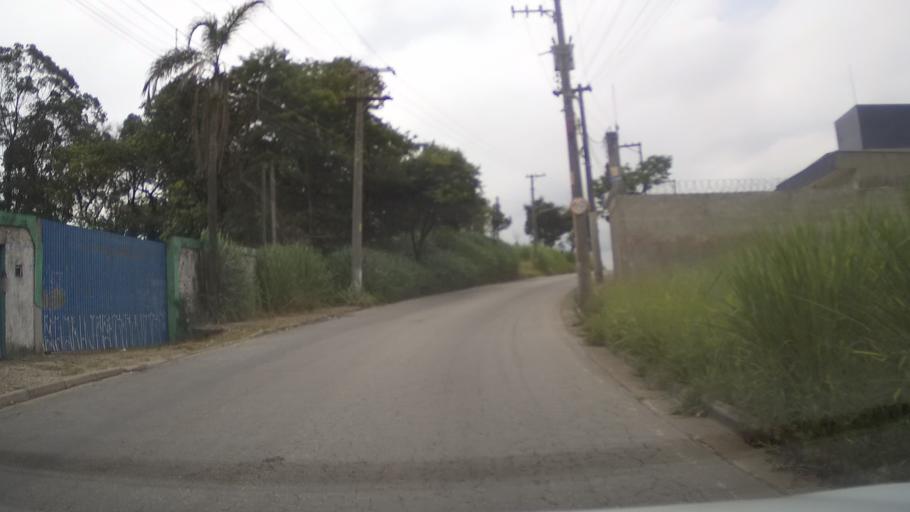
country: BR
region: Sao Paulo
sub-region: Itaquaquecetuba
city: Itaquaquecetuba
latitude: -23.4524
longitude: -46.3846
